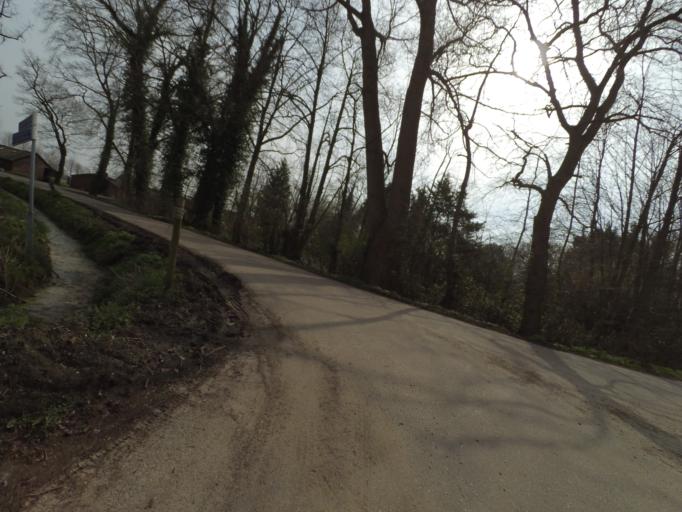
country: NL
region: Gelderland
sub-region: Gemeente Ede
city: Ederveen
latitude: 52.1021
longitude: 5.5726
